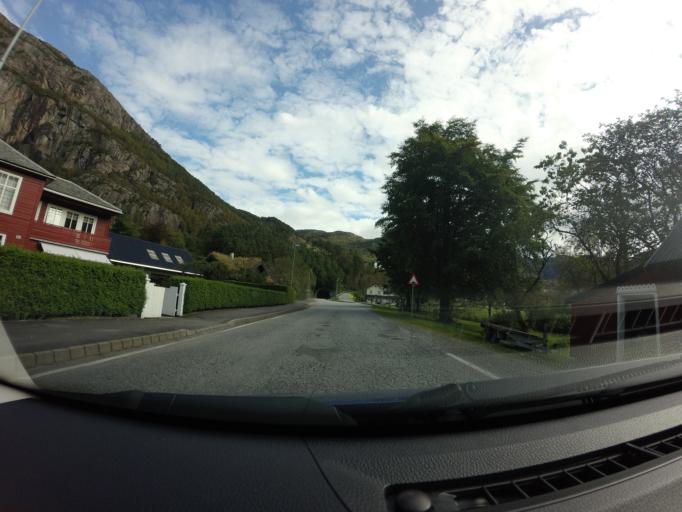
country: NO
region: Rogaland
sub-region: Forsand
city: Forsand
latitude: 58.8069
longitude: 6.2578
